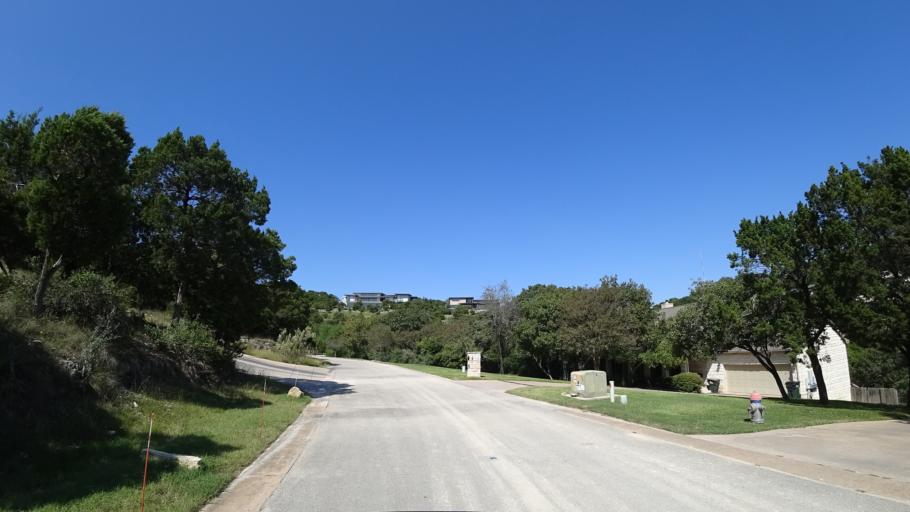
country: US
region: Texas
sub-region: Travis County
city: West Lake Hills
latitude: 30.2961
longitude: -97.8032
